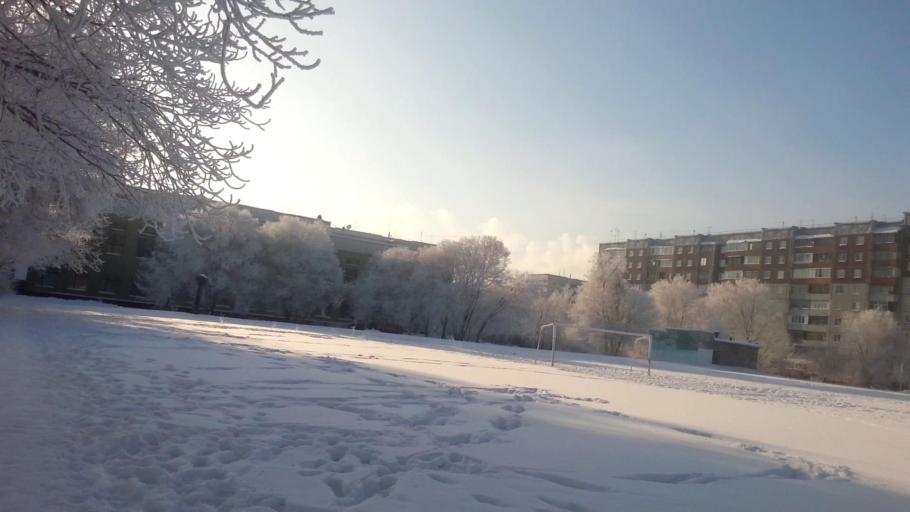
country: RU
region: Altai Krai
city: Novosilikatnyy
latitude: 53.3596
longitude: 83.6650
